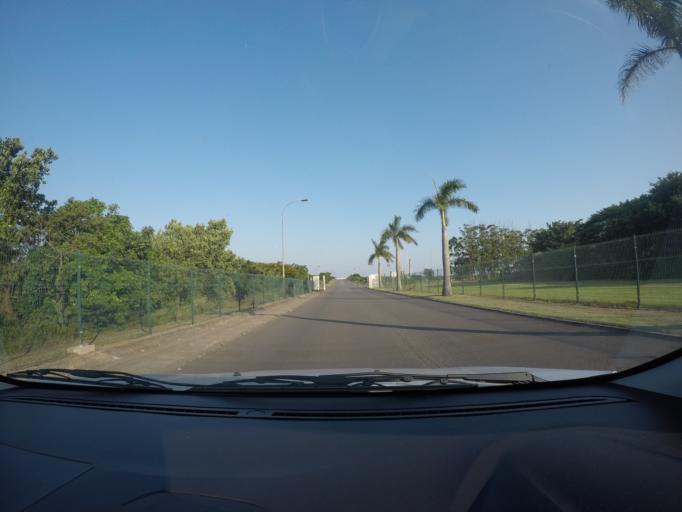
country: ZA
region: KwaZulu-Natal
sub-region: uThungulu District Municipality
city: Richards Bay
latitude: -28.7646
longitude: 31.9992
